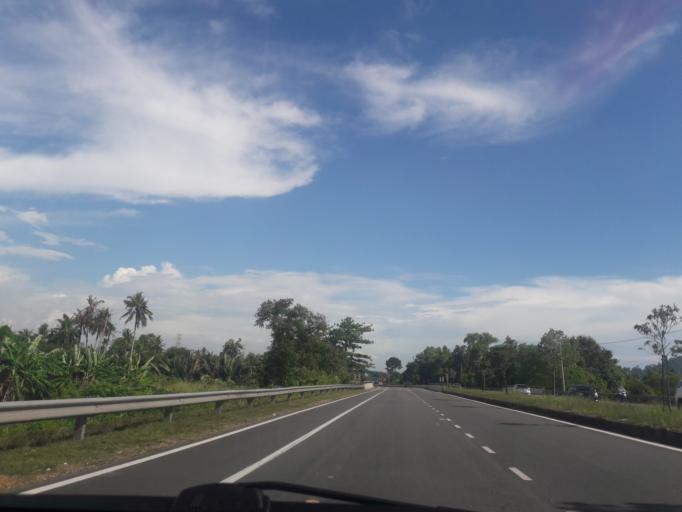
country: MY
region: Kedah
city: Sungai Petani
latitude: 5.6215
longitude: 100.4647
